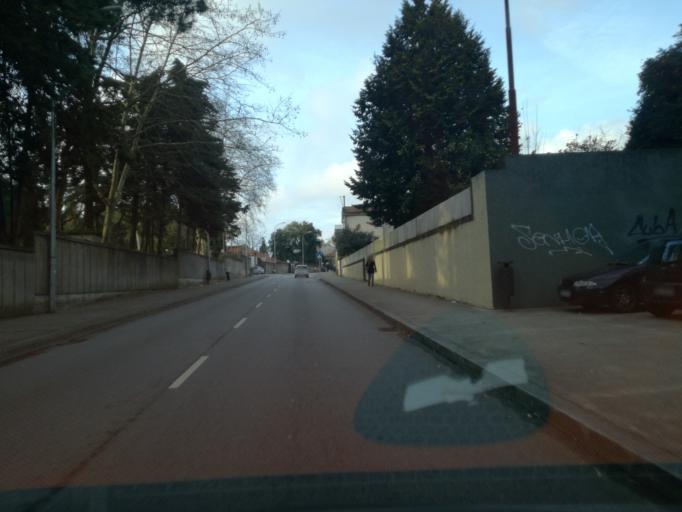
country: PT
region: Porto
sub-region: Matosinhos
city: Senhora da Hora
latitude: 41.1741
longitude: -8.6271
